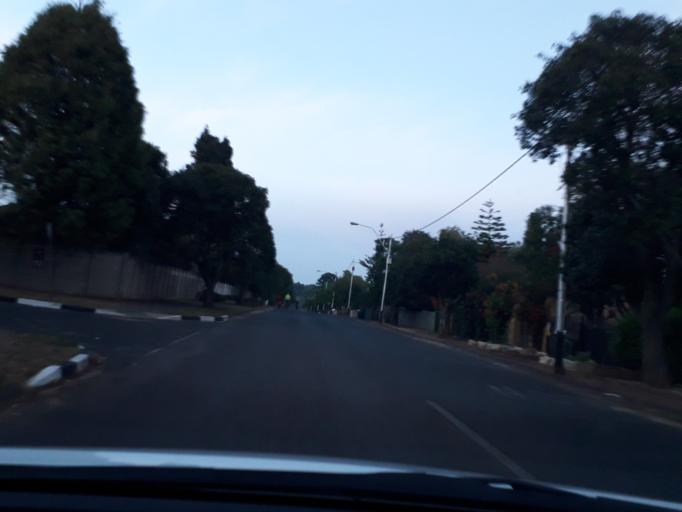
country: ZA
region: Gauteng
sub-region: City of Johannesburg Metropolitan Municipality
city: Johannesburg
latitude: -26.1172
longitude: 28.0007
